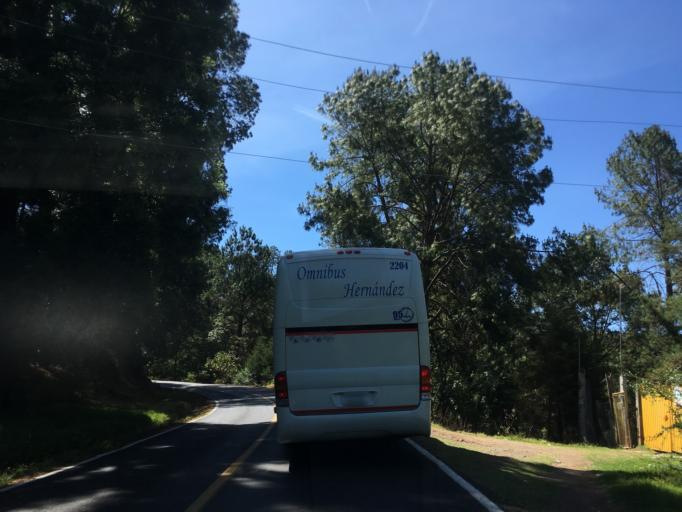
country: MX
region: Michoacan
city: Tzitzio
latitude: 19.6858
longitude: -100.8764
